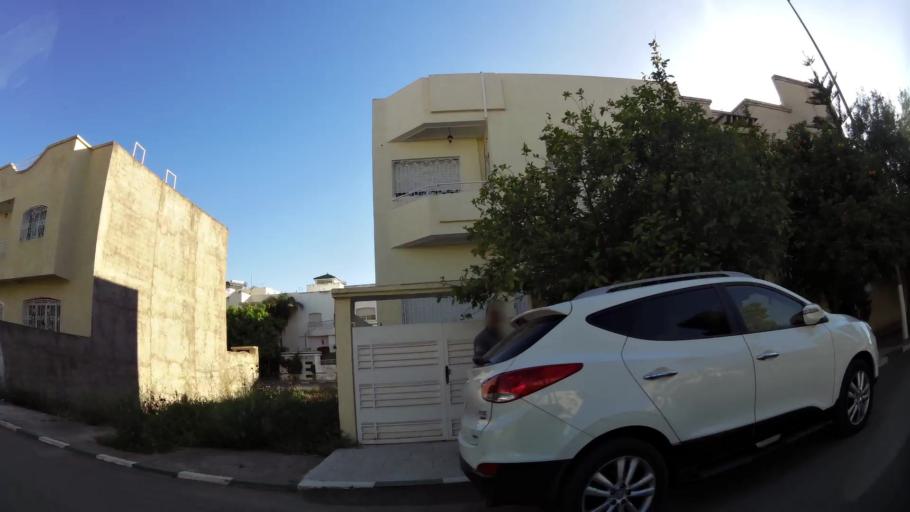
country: MA
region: Fes-Boulemane
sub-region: Fes
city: Fes
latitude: 34.0108
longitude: -5.0136
